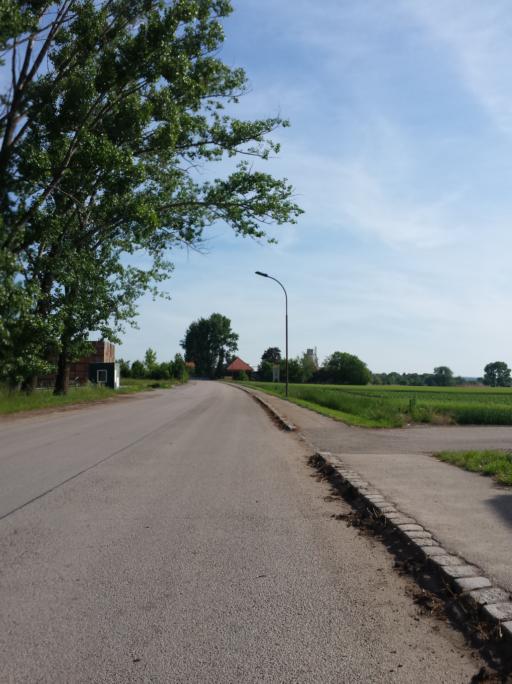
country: AT
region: Lower Austria
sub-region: Politischer Bezirk Hollabrunn
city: Wullersdorf
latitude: 48.6179
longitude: 16.0941
